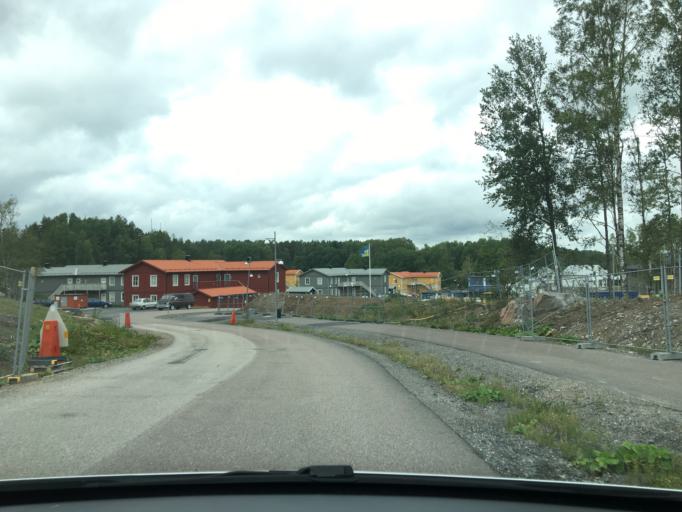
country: SE
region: Vaestra Goetaland
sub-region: Ale Kommun
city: Alvangen
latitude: 57.9489
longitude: 12.1219
